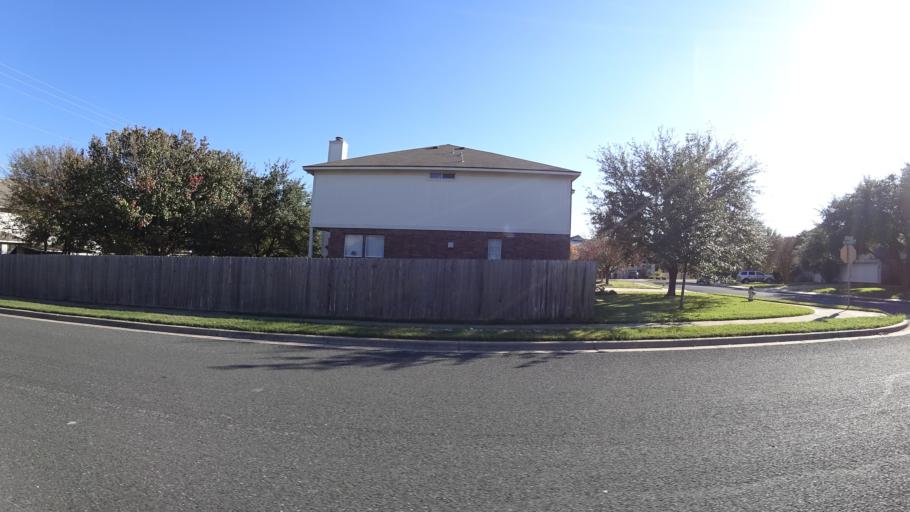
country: US
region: Texas
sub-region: Williamson County
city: Brushy Creek
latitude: 30.4881
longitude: -97.7352
